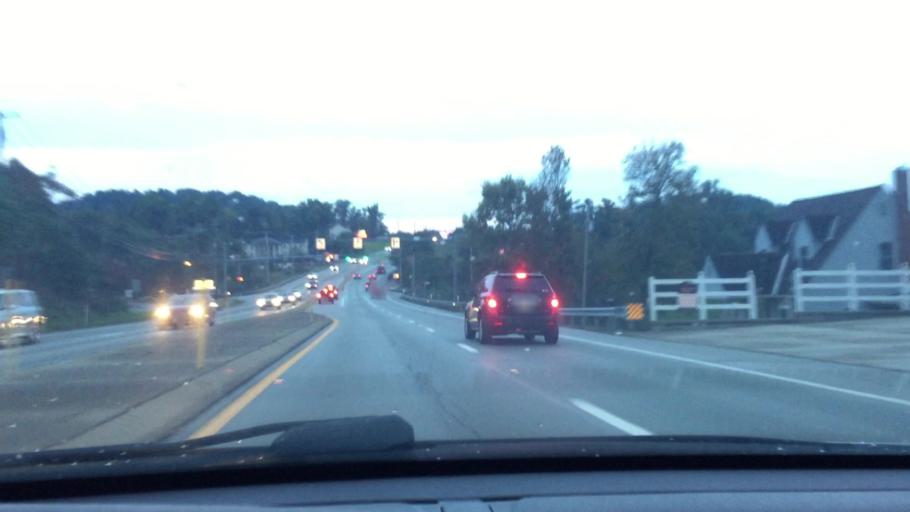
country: US
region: Pennsylvania
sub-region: Washington County
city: McGovern
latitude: 40.2070
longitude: -80.1996
